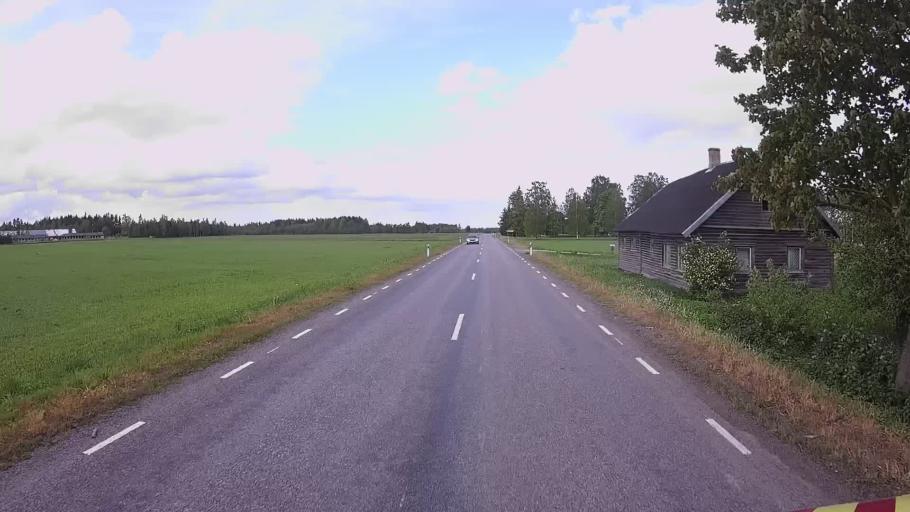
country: EE
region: Jogevamaa
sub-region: Mustvee linn
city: Mustvee
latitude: 58.9985
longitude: 26.8994
